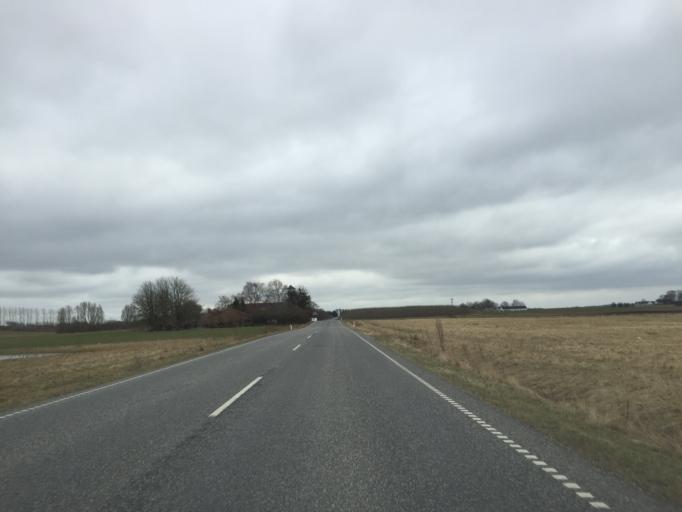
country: DK
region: Capital Region
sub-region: Allerod Kommune
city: Lynge
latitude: 55.8774
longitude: 12.2730
